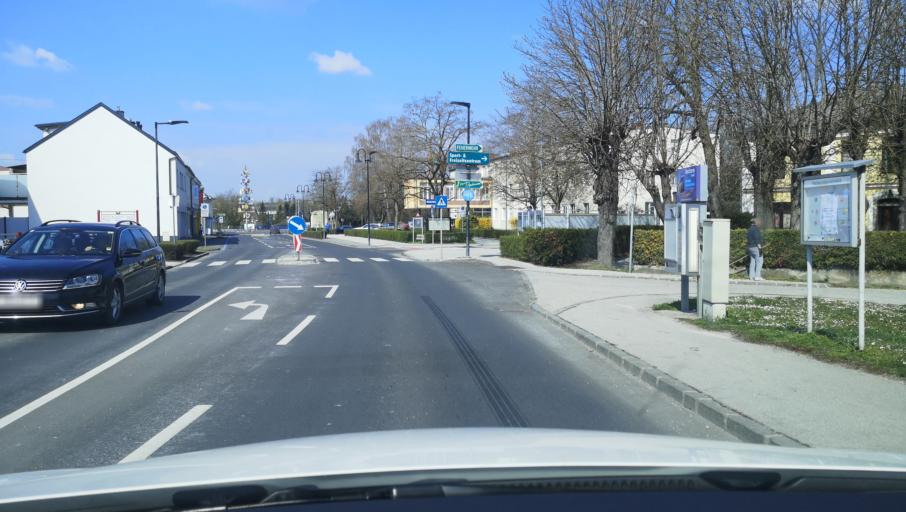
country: AT
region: Lower Austria
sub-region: Politischer Bezirk Amstetten
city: Winklarn
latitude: 48.0763
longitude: 14.8172
